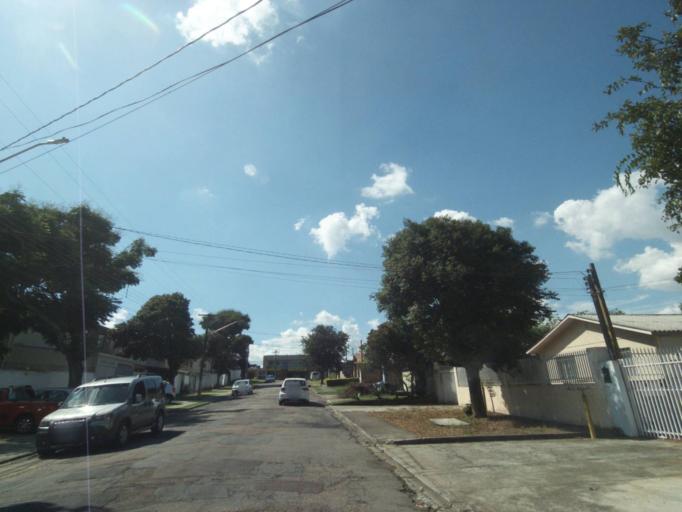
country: BR
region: Parana
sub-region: Pinhais
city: Pinhais
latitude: -25.4555
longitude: -49.2149
